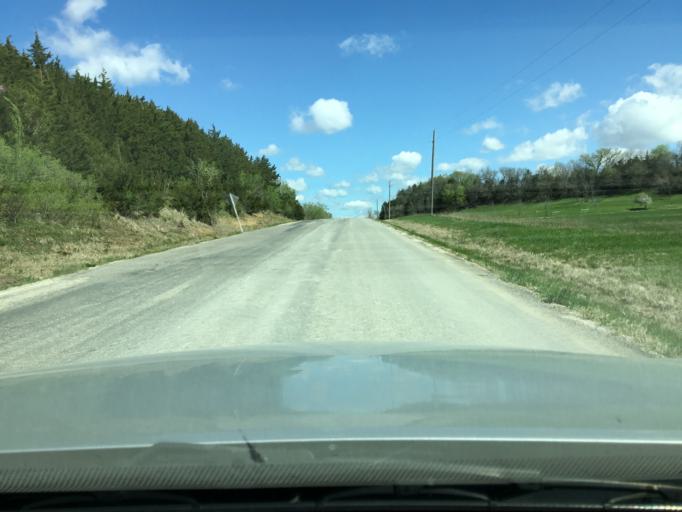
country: US
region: Kansas
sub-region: Anderson County
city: Garnett
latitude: 38.3469
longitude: -95.1259
